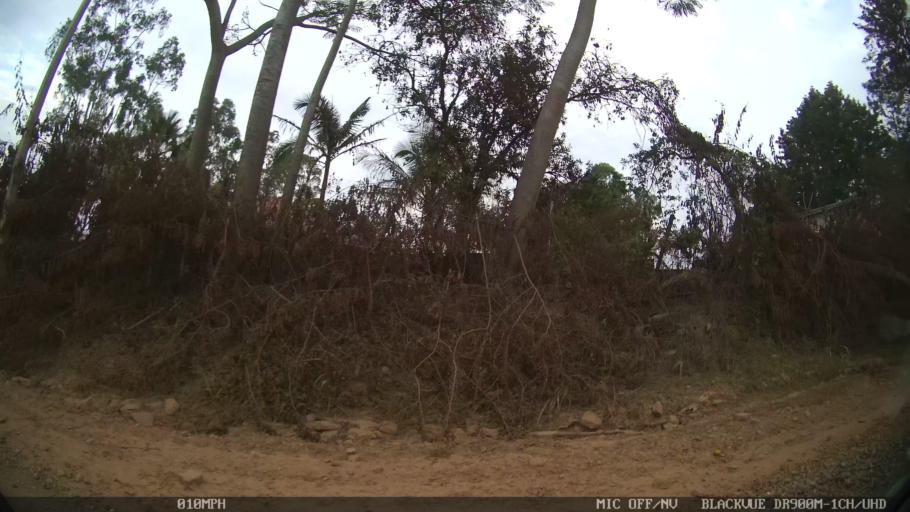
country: BR
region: Sao Paulo
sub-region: Americana
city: Americana
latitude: -22.6818
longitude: -47.3820
